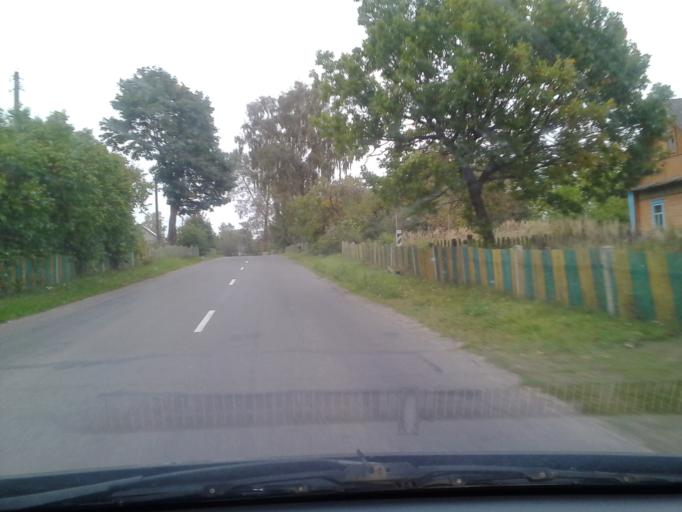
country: BY
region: Vitebsk
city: Pastavy
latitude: 55.1238
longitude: 26.9301
